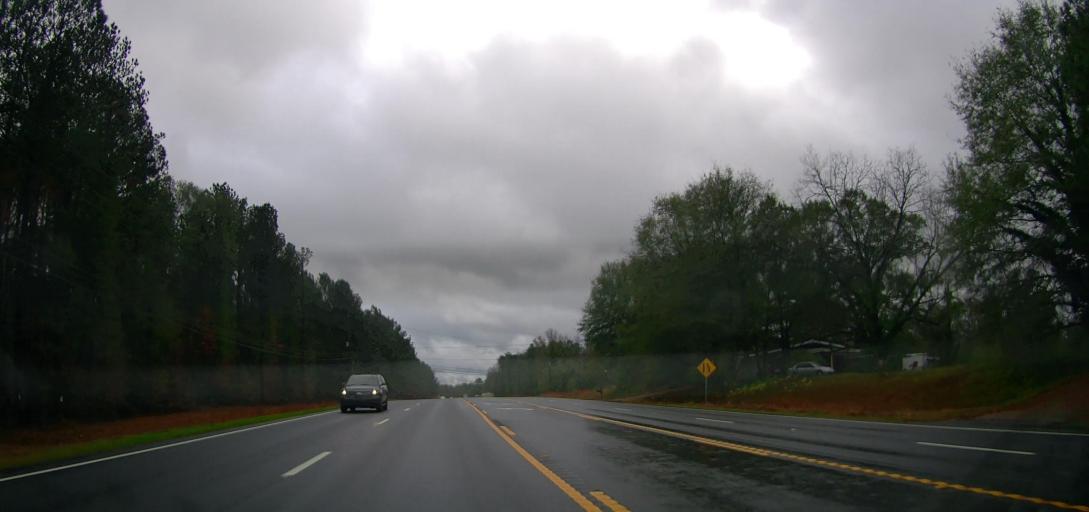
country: US
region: Georgia
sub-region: Clarke County
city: Country Club Estates
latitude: 34.0129
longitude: -83.3874
